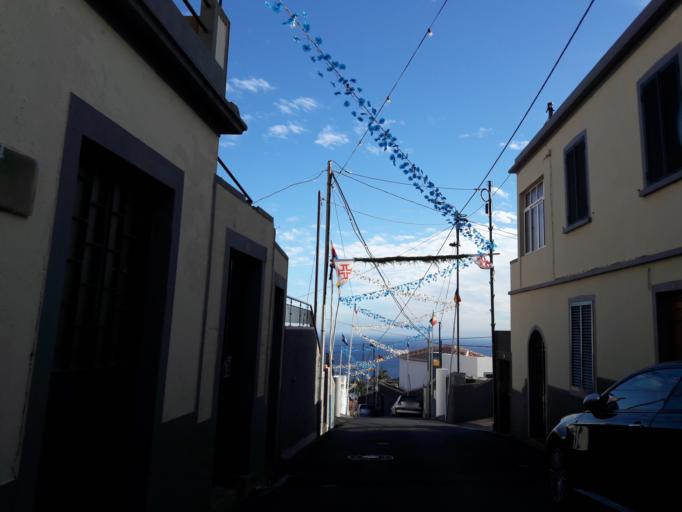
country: PT
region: Madeira
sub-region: Funchal
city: Nossa Senhora do Monte
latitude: 32.6638
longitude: -16.9226
